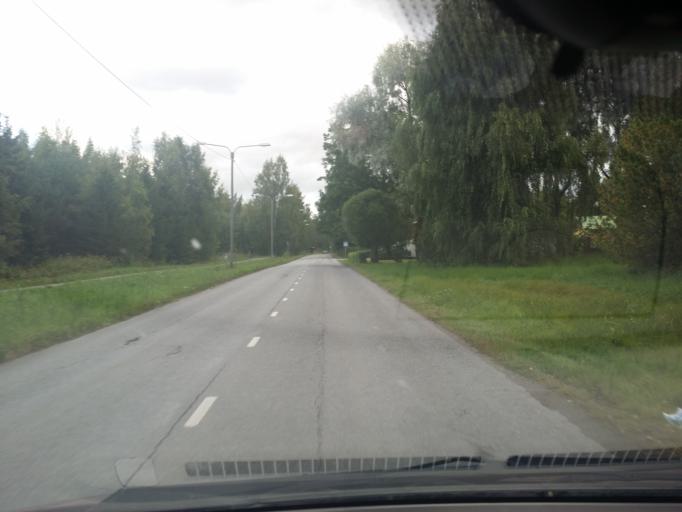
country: FI
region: Satakunta
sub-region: Pori
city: Pori
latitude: 61.5012
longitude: 21.8036
